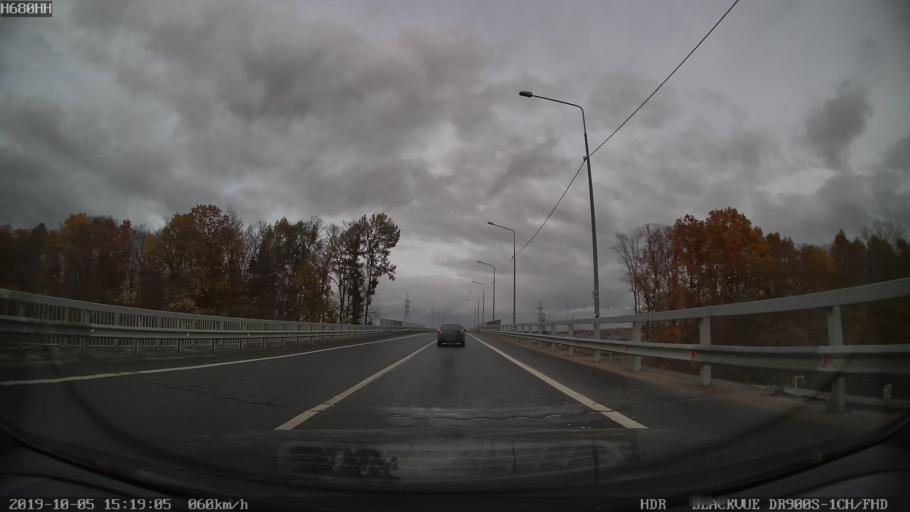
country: RU
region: Moskovskaya
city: Solnechnogorsk
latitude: 56.2177
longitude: 36.9032
